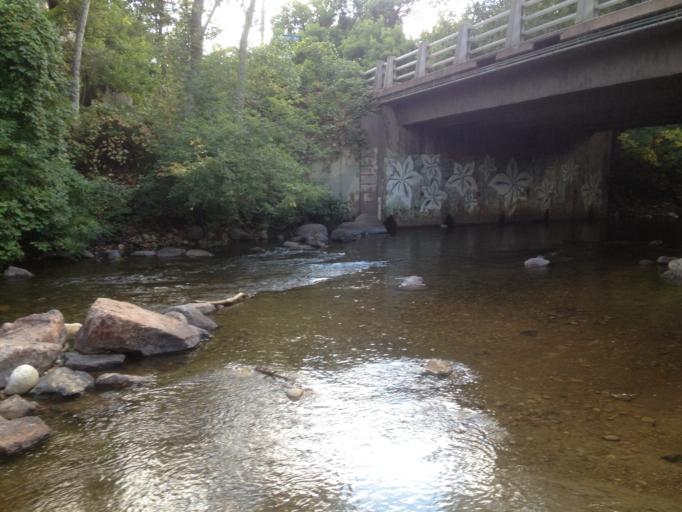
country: US
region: Colorado
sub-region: Boulder County
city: Boulder
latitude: 40.0138
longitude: -105.2871
